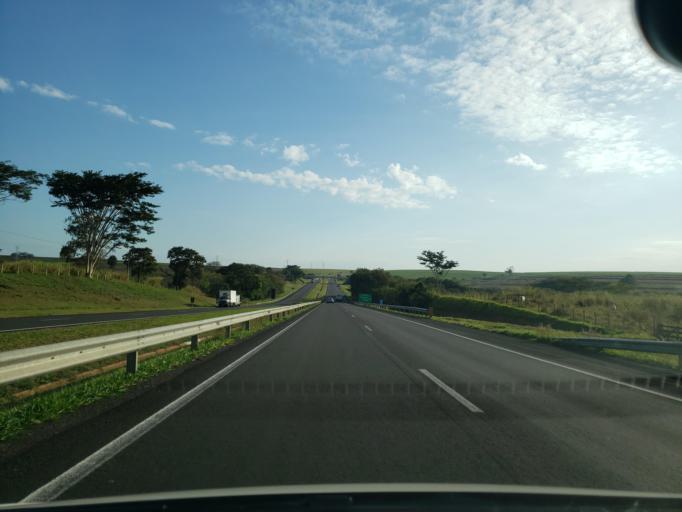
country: BR
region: Sao Paulo
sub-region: Valparaiso
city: Valparaiso
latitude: -21.2132
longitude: -50.8334
